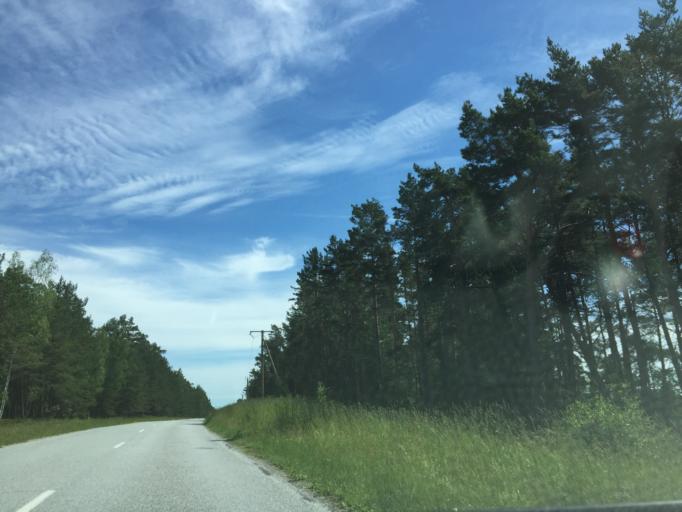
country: LV
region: Talsu Rajons
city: Valdemarpils
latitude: 57.5868
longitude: 22.6151
